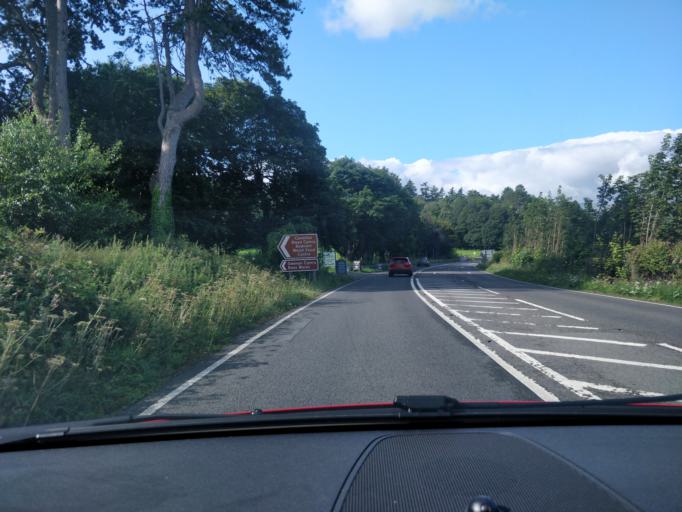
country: GB
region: Wales
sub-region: Conwy
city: Llansantffraid Glan Conwy
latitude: 53.2327
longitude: -3.8074
